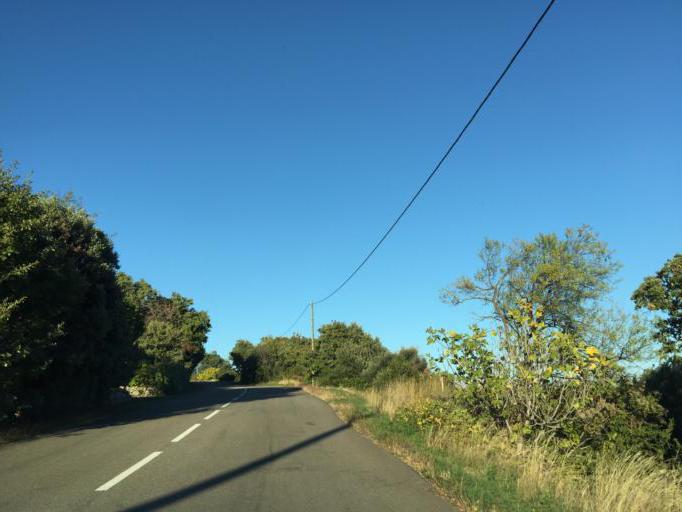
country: FR
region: Rhone-Alpes
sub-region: Departement de l'Ardeche
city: Bourg-Saint-Andeol
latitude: 44.4124
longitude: 4.5148
